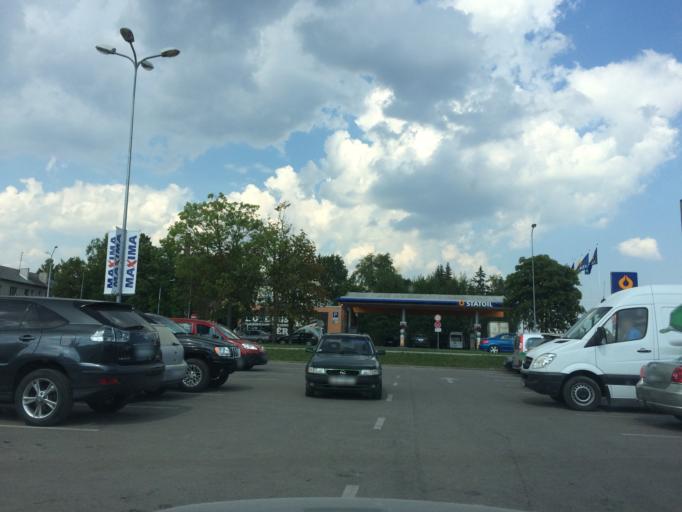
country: LV
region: Rezekne
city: Rezekne
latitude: 56.5235
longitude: 27.3408
